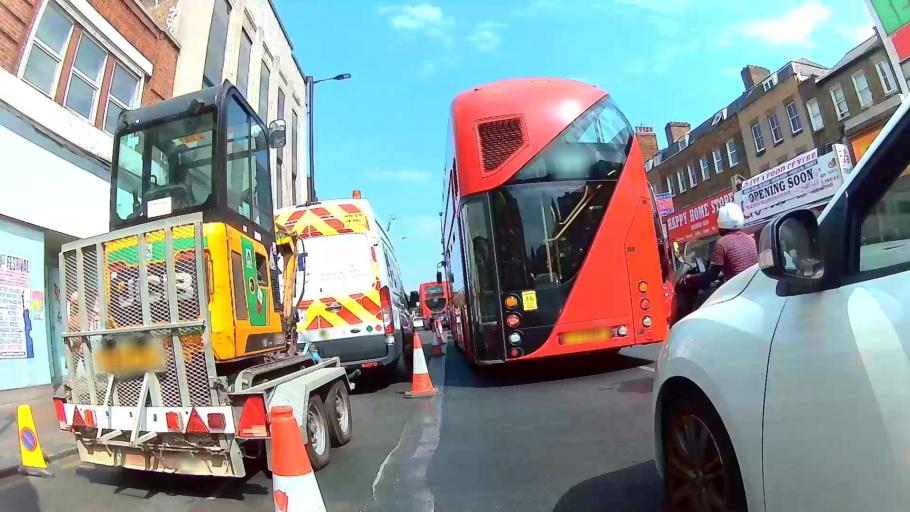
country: GB
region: England
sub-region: Greater London
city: Enfield
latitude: 51.6135
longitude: -0.0645
